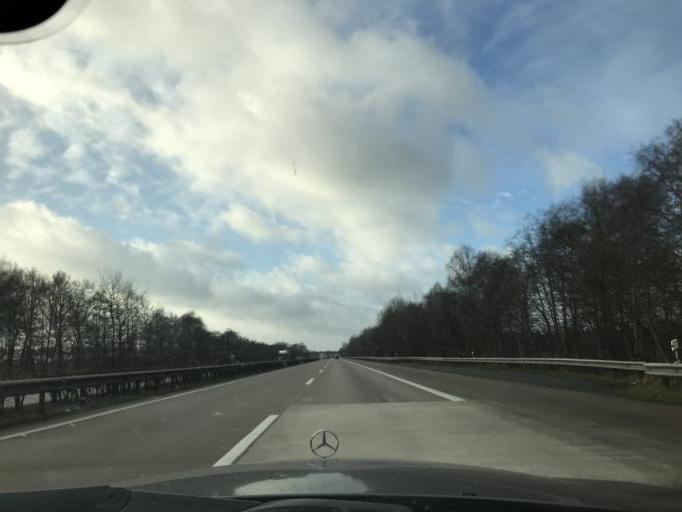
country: DE
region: Lower Saxony
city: Gross Ippener
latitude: 52.9857
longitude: 8.6412
